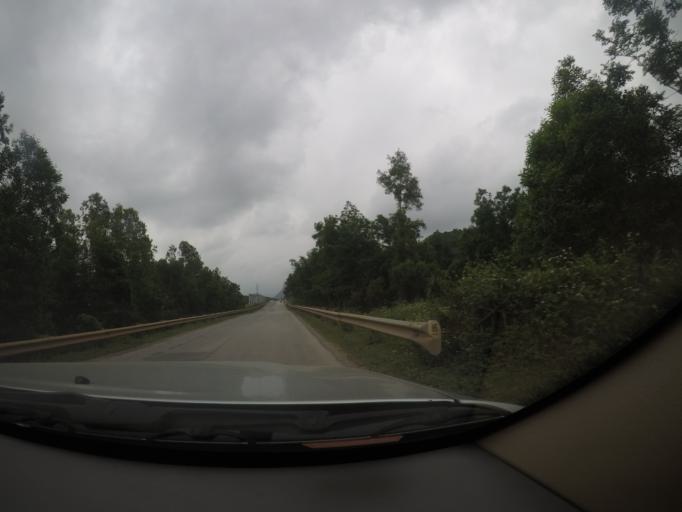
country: VN
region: Quang Binh
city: Quan Hau
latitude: 17.3276
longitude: 106.6241
